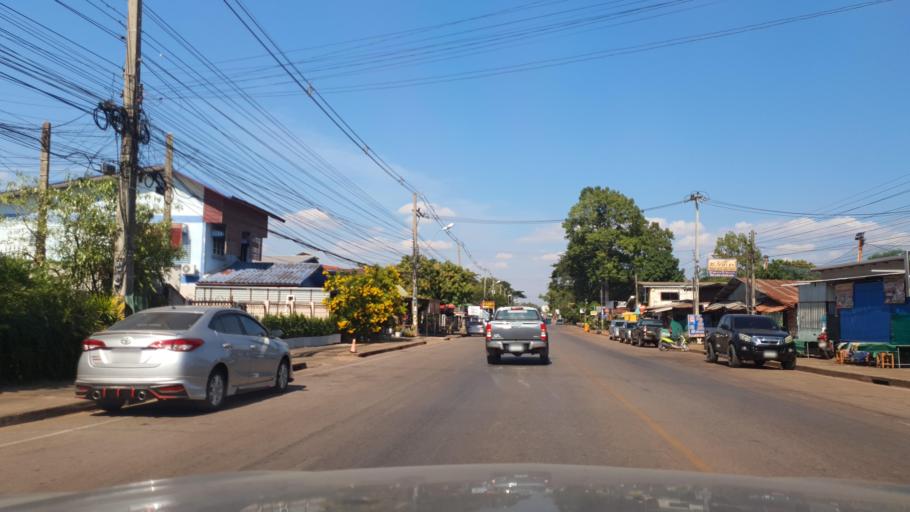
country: TH
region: Sakon Nakhon
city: Sakon Nakhon
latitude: 17.1659
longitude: 104.1241
